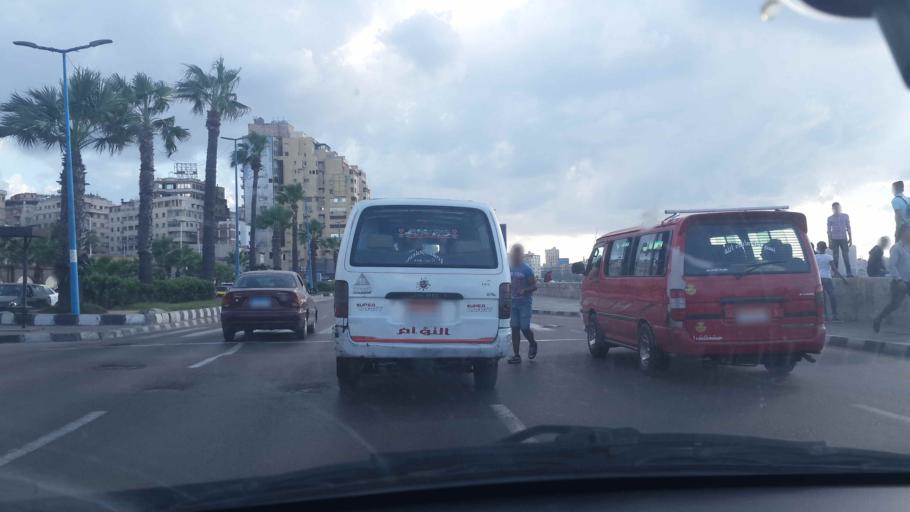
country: EG
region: Alexandria
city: Alexandria
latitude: 31.2082
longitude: 29.9068
